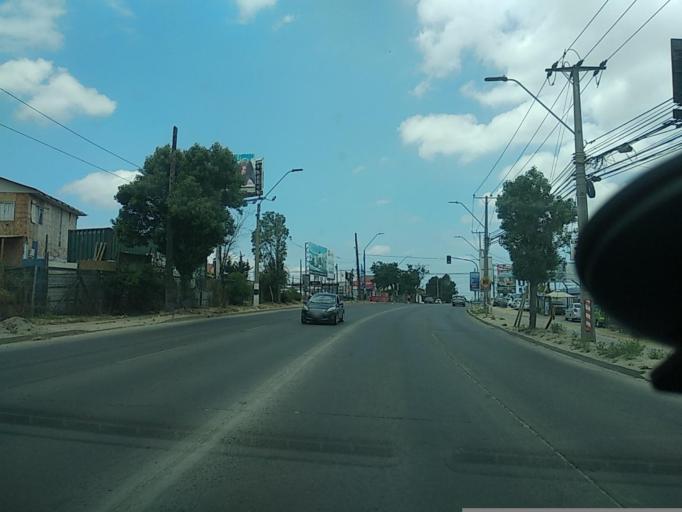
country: CL
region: Valparaiso
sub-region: Provincia de Marga Marga
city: Villa Alemana
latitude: -33.0461
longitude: -71.3974
